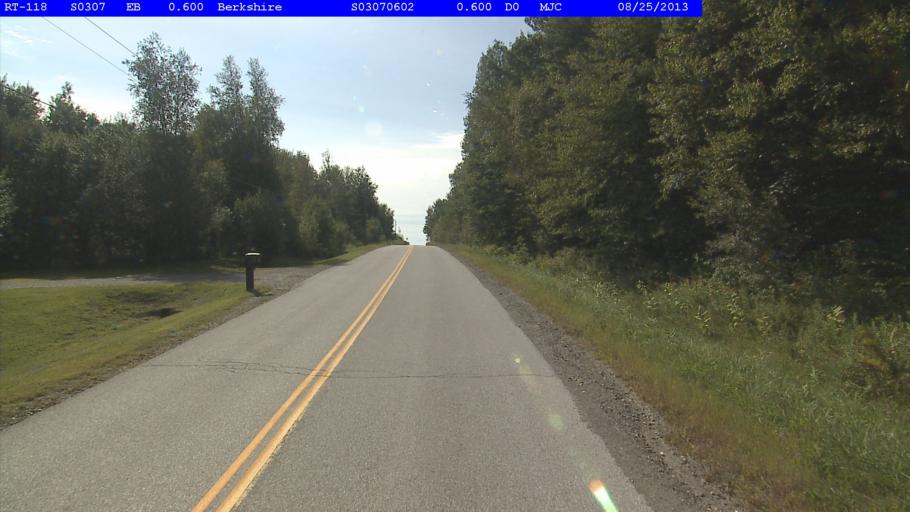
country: US
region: Vermont
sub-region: Franklin County
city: Richford
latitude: 44.9356
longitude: -72.7233
